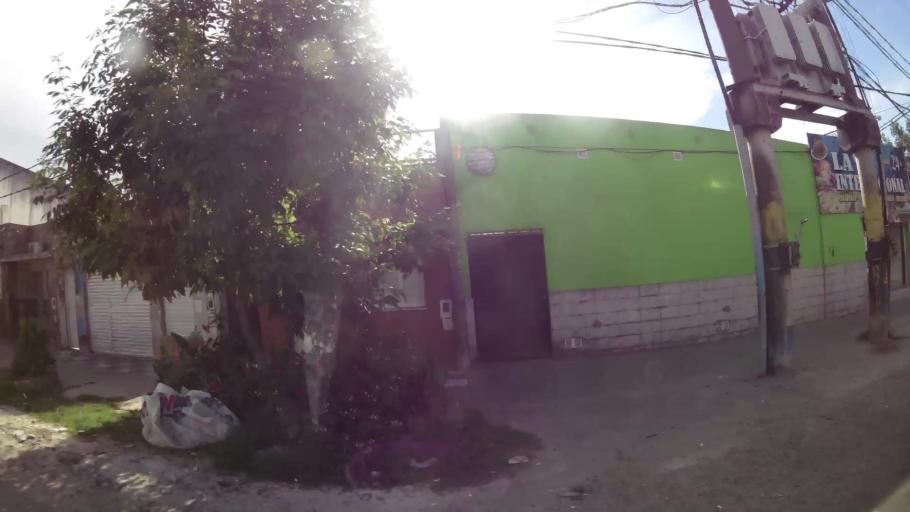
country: AR
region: Santa Fe
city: Granadero Baigorria
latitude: -32.9203
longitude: -60.7077
